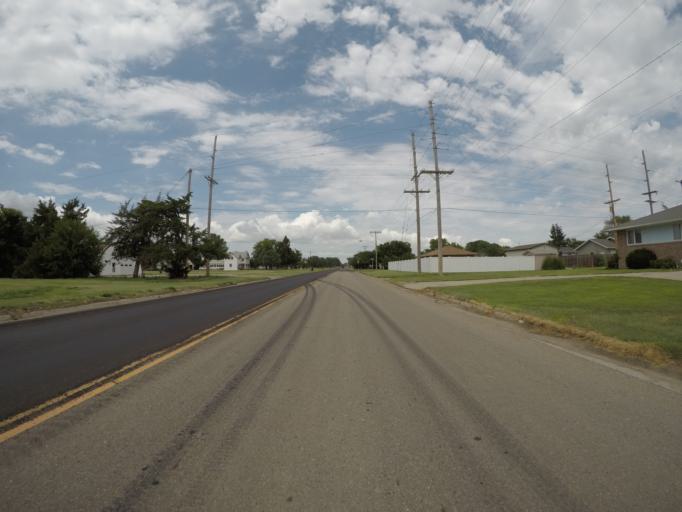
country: US
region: Kansas
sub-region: Rawlins County
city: Atwood
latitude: 39.8027
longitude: -101.0469
